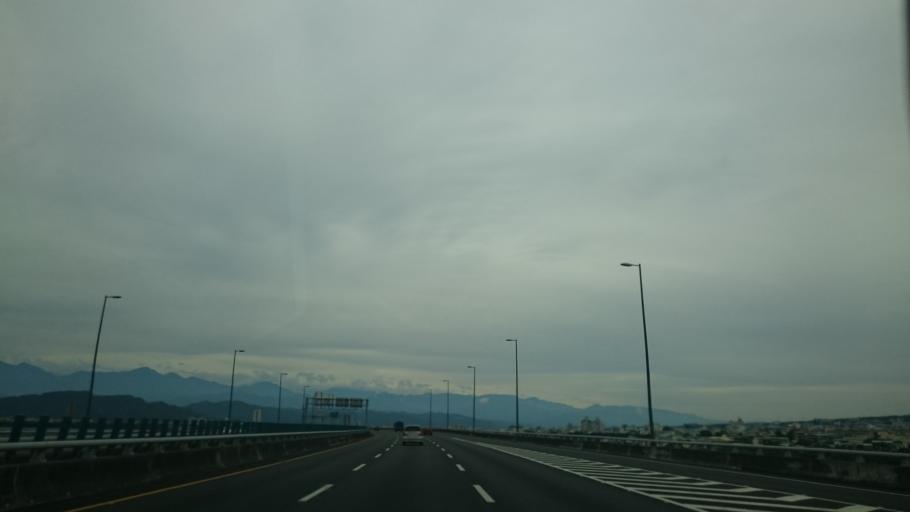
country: TW
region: Taiwan
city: Zhongxing New Village
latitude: 23.9444
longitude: 120.6709
